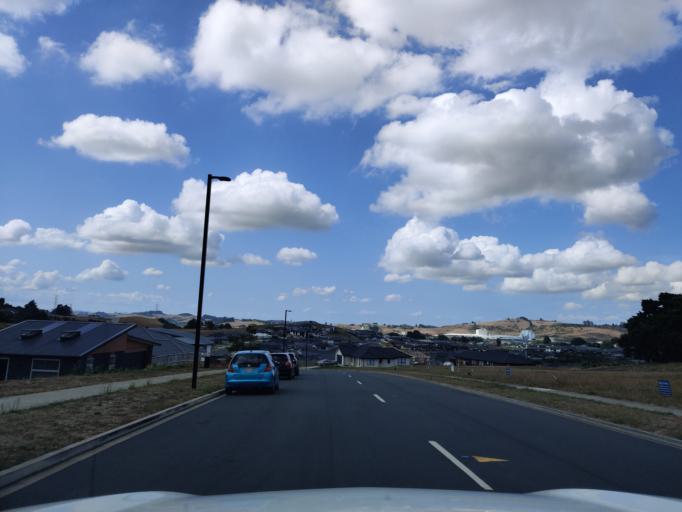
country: NZ
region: Auckland
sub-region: Auckland
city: Pukekohe East
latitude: -37.2342
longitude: 175.0147
